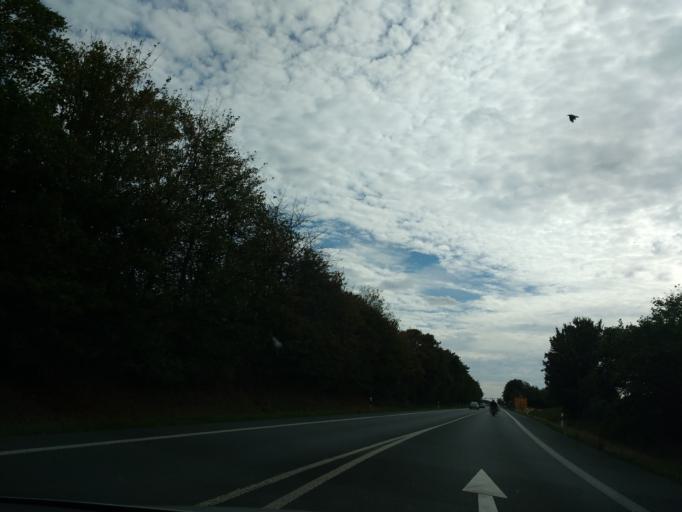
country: DE
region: North Rhine-Westphalia
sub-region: Regierungsbezirk Arnsberg
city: Anrochte
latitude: 51.5718
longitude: 8.3100
